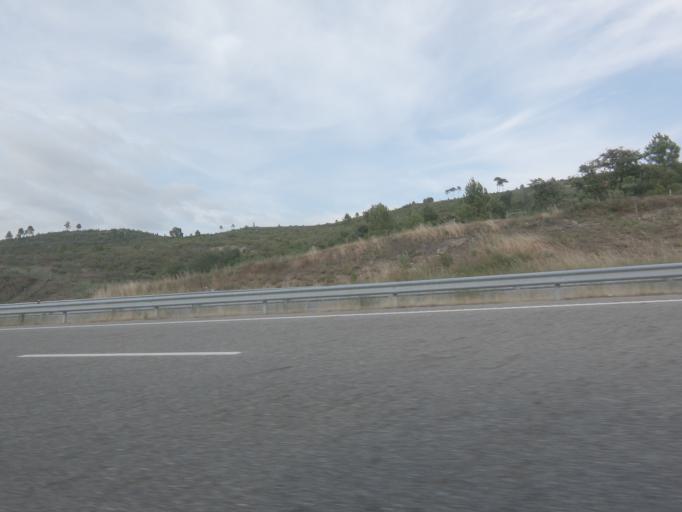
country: PT
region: Vila Real
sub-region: Boticas
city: Boticas
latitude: 41.6287
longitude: -7.5956
